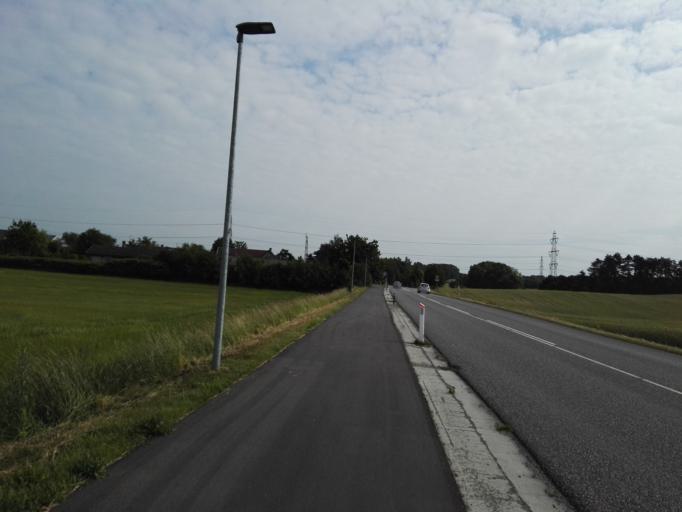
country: DK
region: Zealand
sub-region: Roskilde Kommune
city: Jyllinge
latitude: 55.7668
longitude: 12.1219
